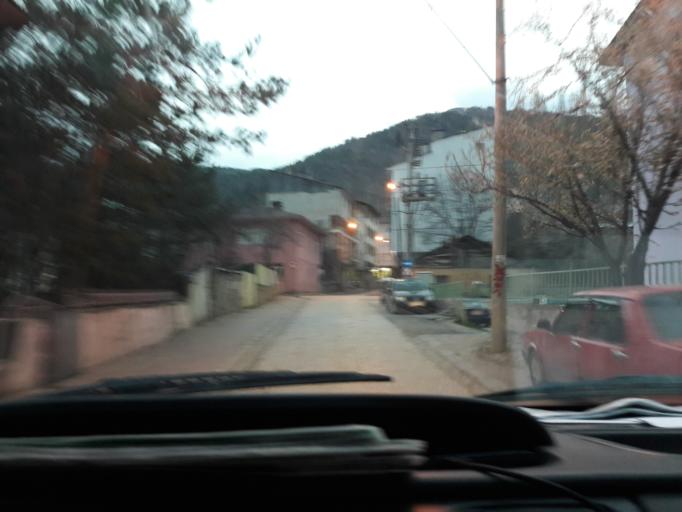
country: TR
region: Giresun
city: Alucra
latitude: 40.3214
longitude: 38.7645
